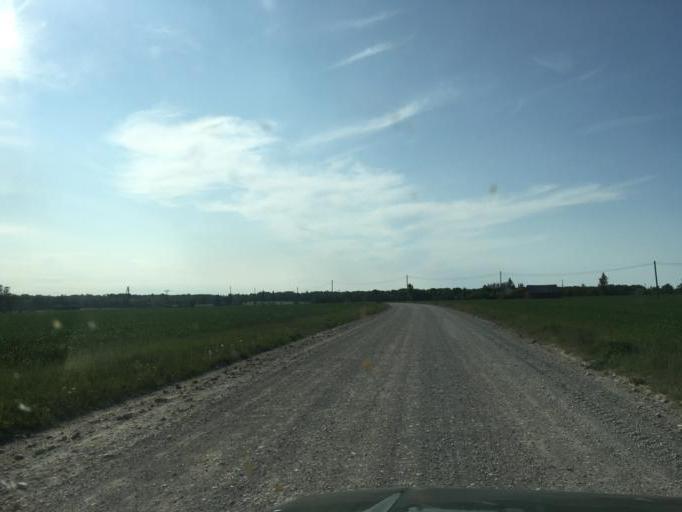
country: LV
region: Dundaga
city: Dundaga
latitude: 57.6222
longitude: 22.4096
